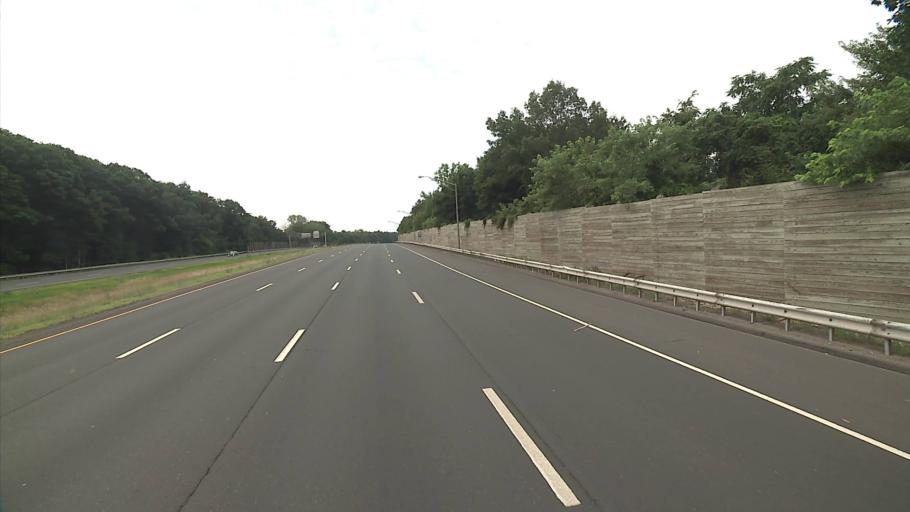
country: US
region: Connecticut
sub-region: Hartford County
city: Plainville
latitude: 41.6631
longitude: -72.8479
